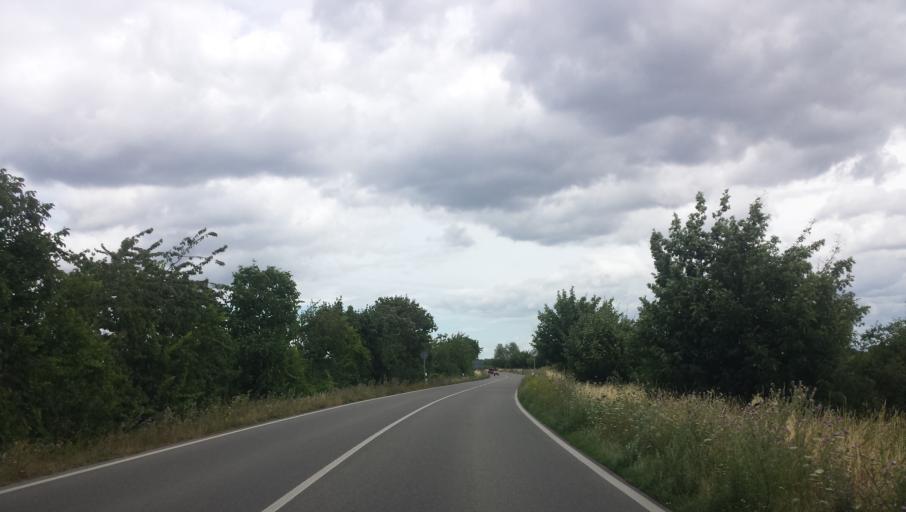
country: DE
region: Rheinland-Pfalz
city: Deidesheim
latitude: 49.3876
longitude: 8.1784
